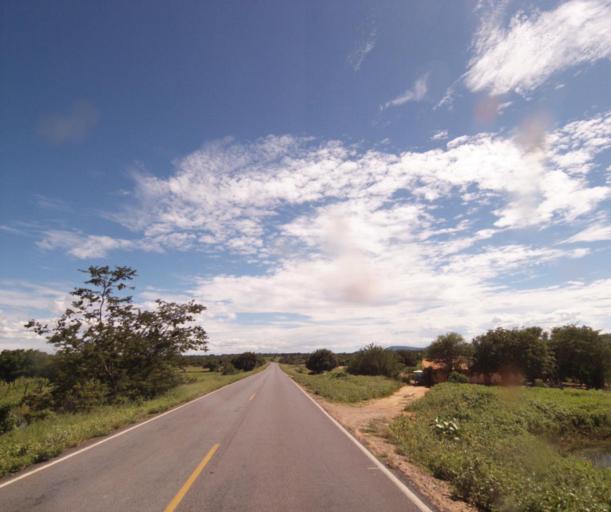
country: BR
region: Bahia
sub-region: Guanambi
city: Guanambi
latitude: -14.5564
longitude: -42.7020
